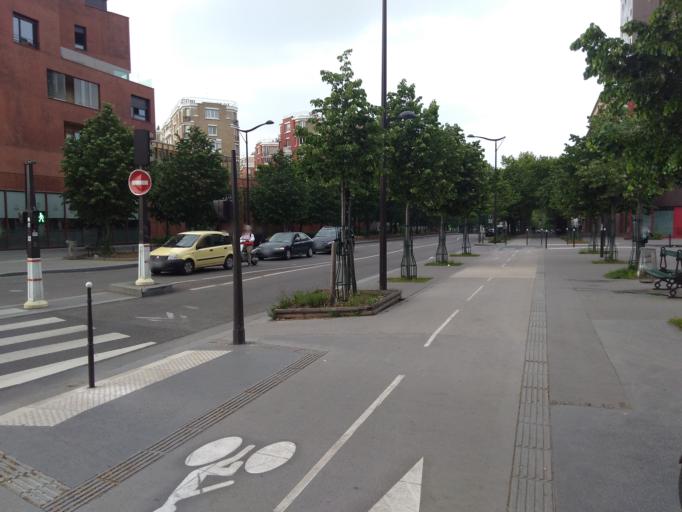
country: FR
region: Ile-de-France
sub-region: Departement du Val-de-Marne
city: Le Kremlin-Bicetre
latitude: 48.8206
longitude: 2.3718
